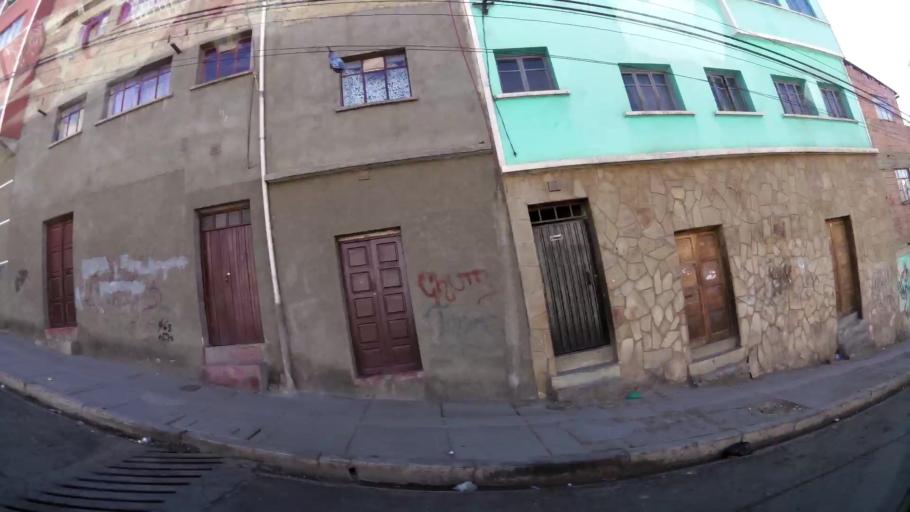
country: BO
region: La Paz
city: La Paz
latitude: -16.5026
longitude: -68.1466
